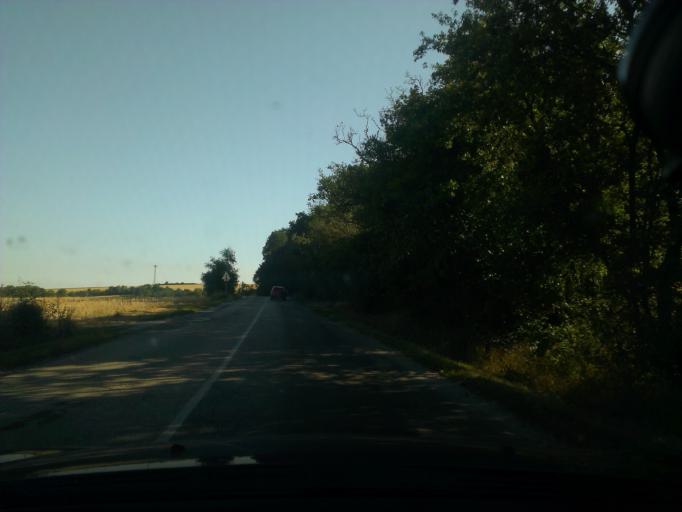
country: SK
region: Trnavsky
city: Vrbove
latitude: 48.6737
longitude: 17.6918
